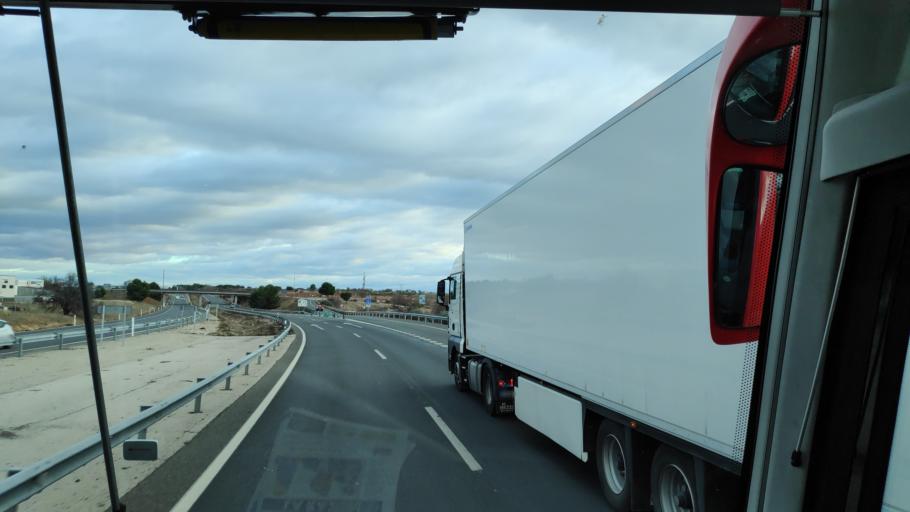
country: ES
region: Madrid
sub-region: Provincia de Madrid
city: Villarejo de Salvanes
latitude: 40.1743
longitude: -3.2951
